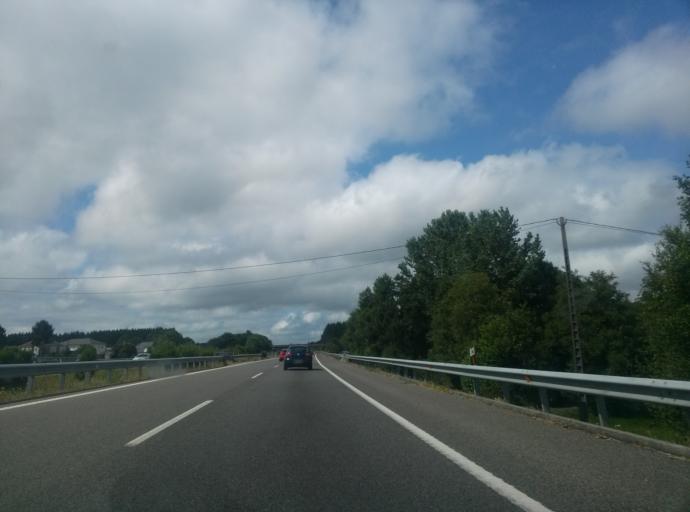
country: ES
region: Galicia
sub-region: Provincia de Lugo
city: Outeiro de Rei
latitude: 43.0777
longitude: -7.5782
